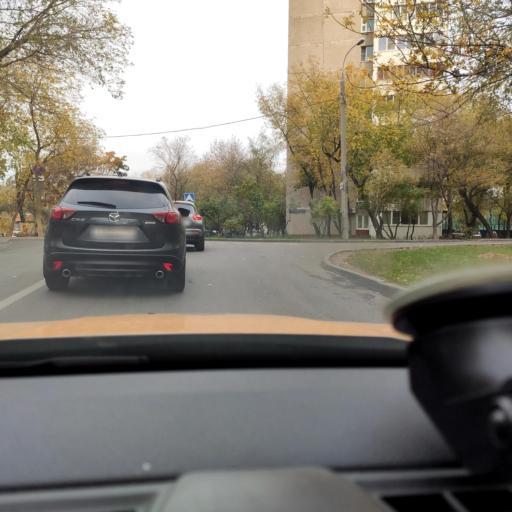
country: RU
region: Moscow
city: Tekstil'shchiki
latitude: 55.7052
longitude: 37.7391
